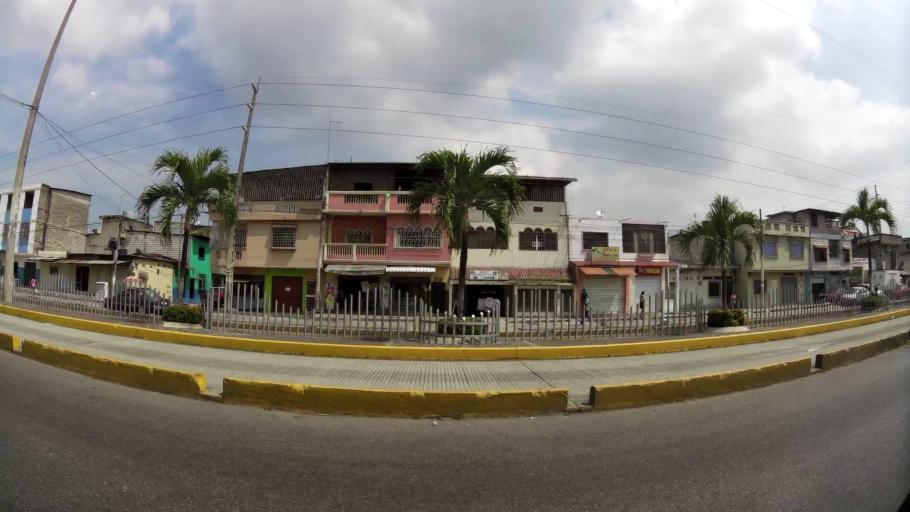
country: EC
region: Guayas
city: Guayaquil
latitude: -2.2466
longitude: -79.8903
